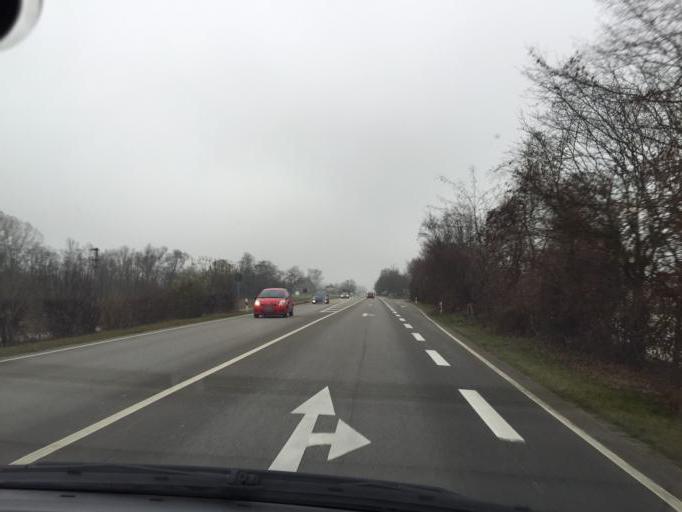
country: DE
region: Baden-Wuerttemberg
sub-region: Freiburg Region
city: Ihringen
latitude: 48.0019
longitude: 7.6245
